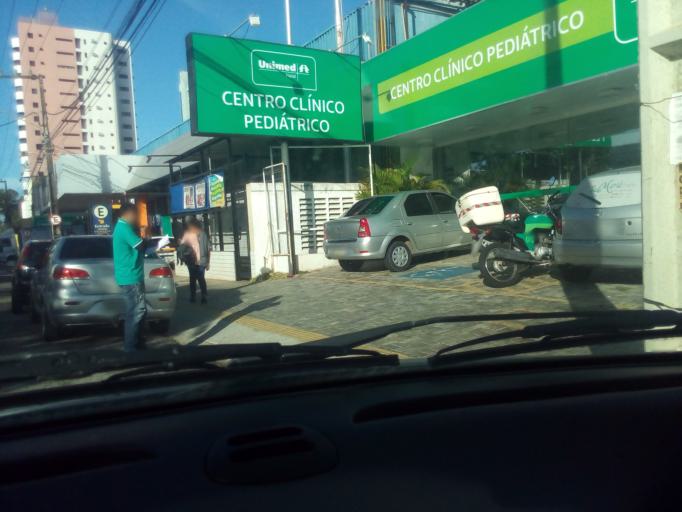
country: BR
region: Rio Grande do Norte
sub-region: Natal
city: Natal
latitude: -5.7845
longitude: -35.2031
